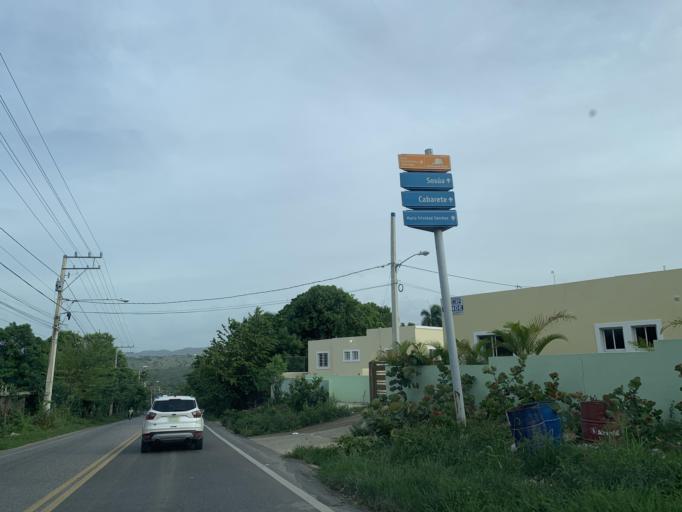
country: DO
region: Puerto Plata
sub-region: Puerto Plata
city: Puerto Plata
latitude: 19.7229
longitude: -70.6216
